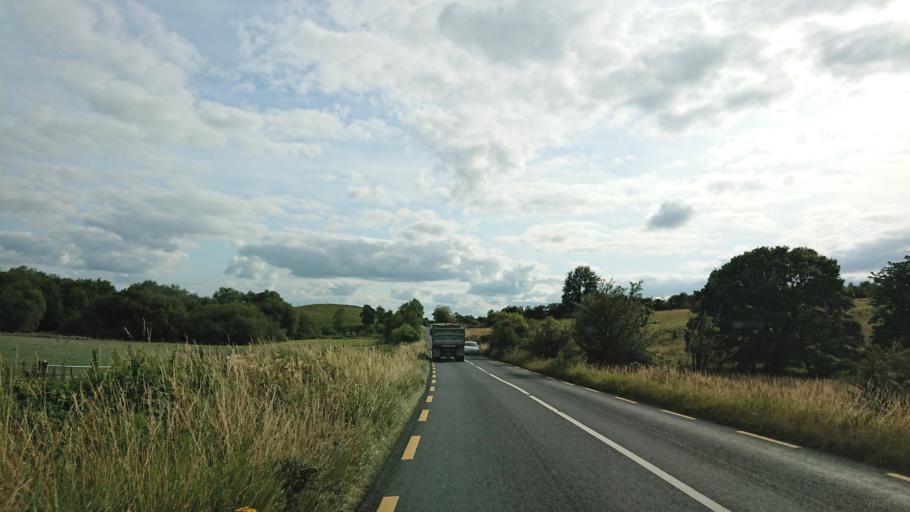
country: IE
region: Connaught
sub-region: County Leitrim
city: Carrick-on-Shannon
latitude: 53.9624
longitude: -8.0761
